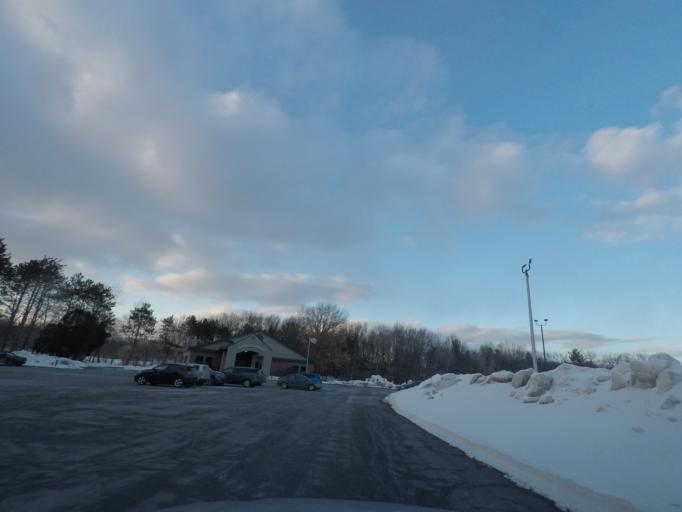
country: US
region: New York
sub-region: Schenectady County
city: Scotia
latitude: 42.8514
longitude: -73.9462
